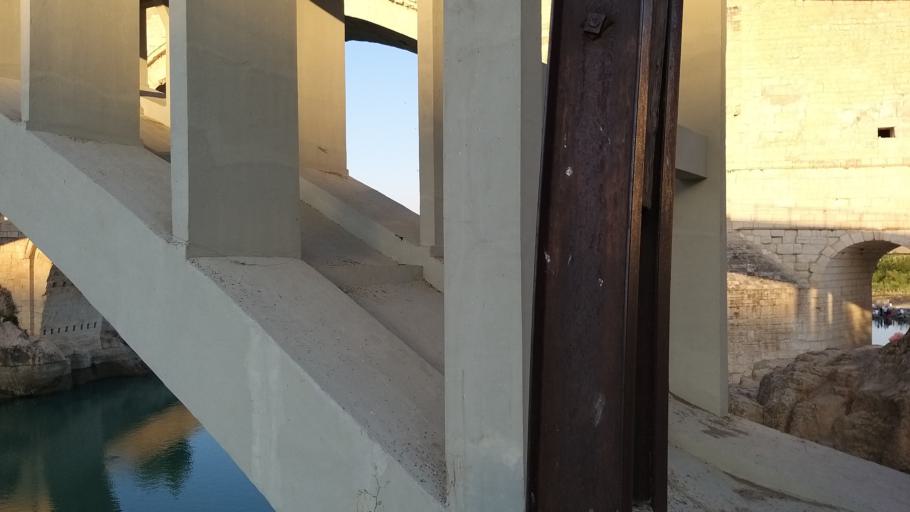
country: TR
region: Diyarbakir
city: Malabadi
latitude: 38.1537
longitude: 41.2033
